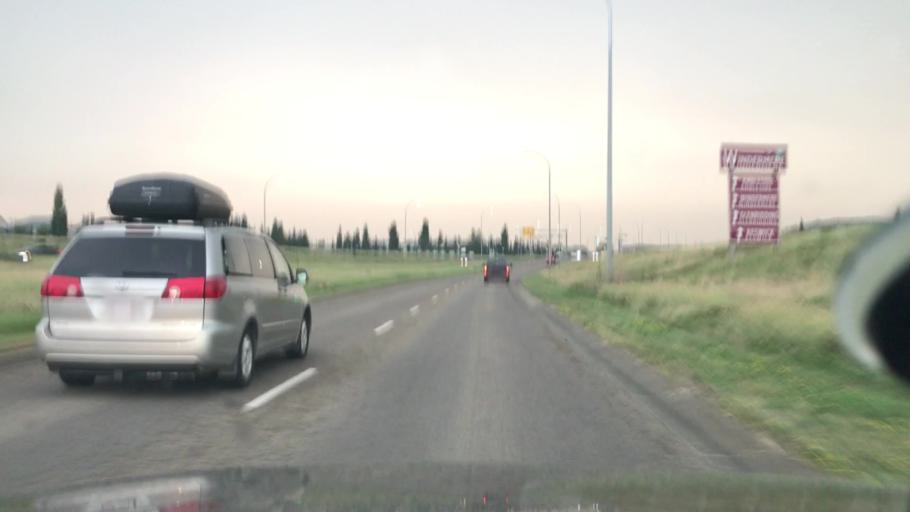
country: CA
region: Alberta
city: Edmonton
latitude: 53.4541
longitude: -113.5900
